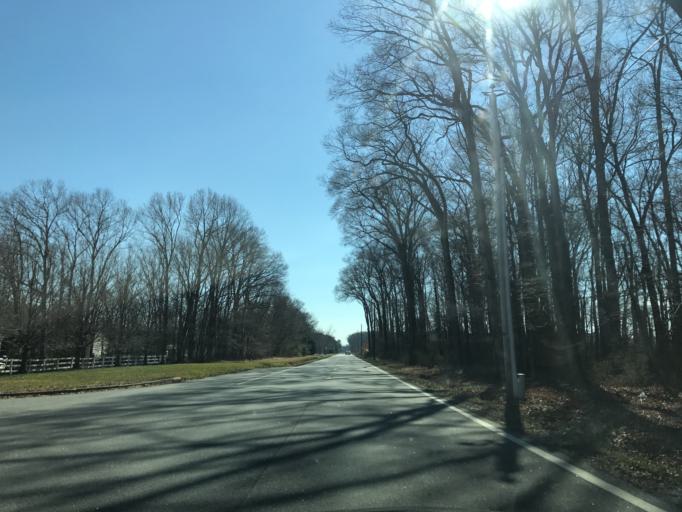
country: US
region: Maryland
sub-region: Queen Anne's County
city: Stevensville
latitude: 39.0028
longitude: -76.3118
